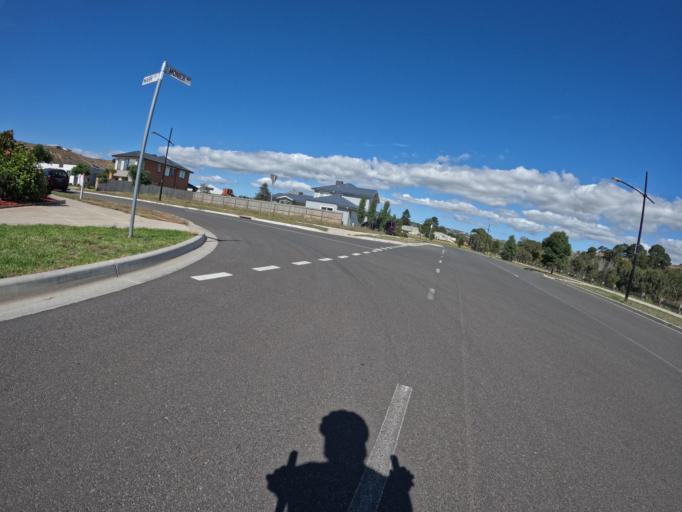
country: AU
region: Victoria
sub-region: Greater Geelong
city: Hamlyn Heights
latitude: -38.1388
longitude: 144.3103
